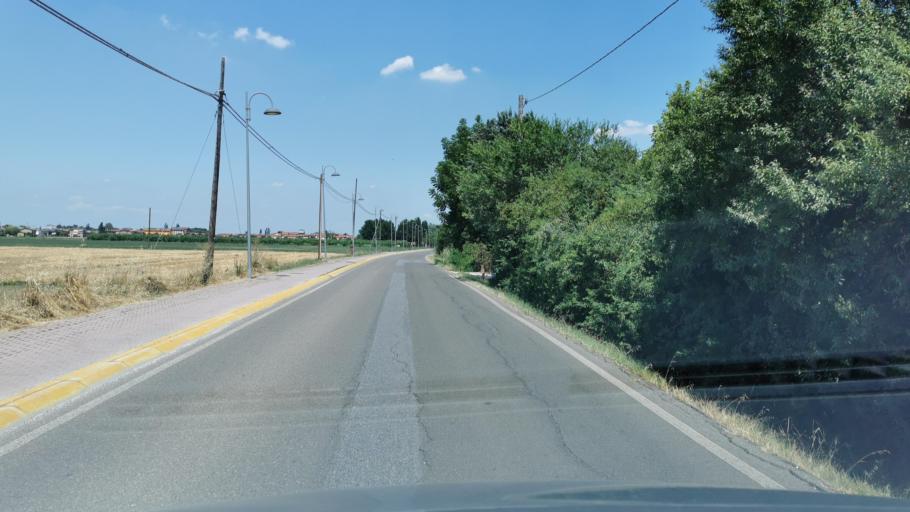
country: IT
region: Emilia-Romagna
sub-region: Provincia di Modena
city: Fossoli
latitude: 44.8092
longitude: 10.8893
